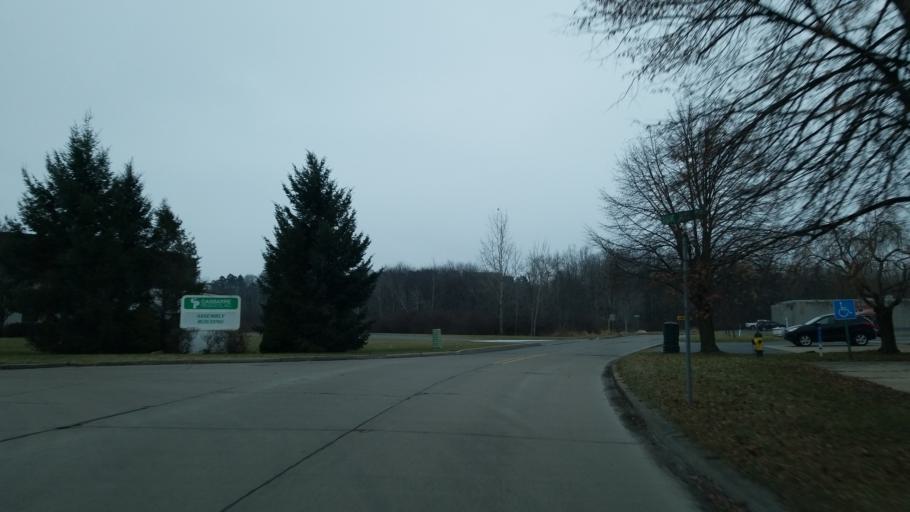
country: US
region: Pennsylvania
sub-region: Clearfield County
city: DuBois
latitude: 41.1213
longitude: -78.7492
